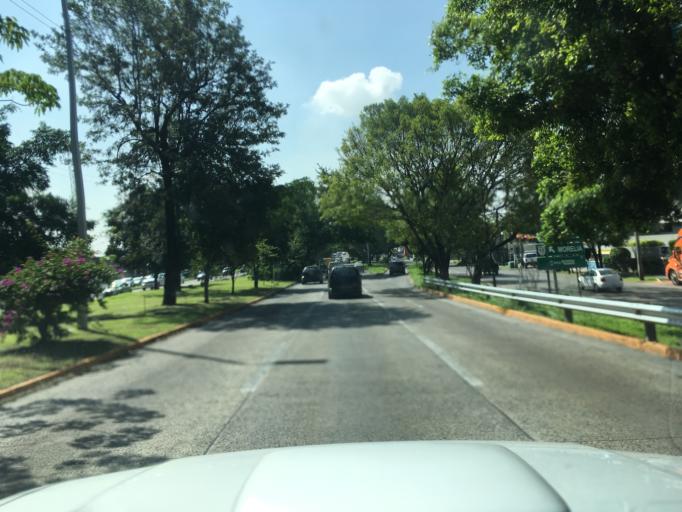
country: MX
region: Jalisco
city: Guadalajara
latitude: 20.6523
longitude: -103.3710
